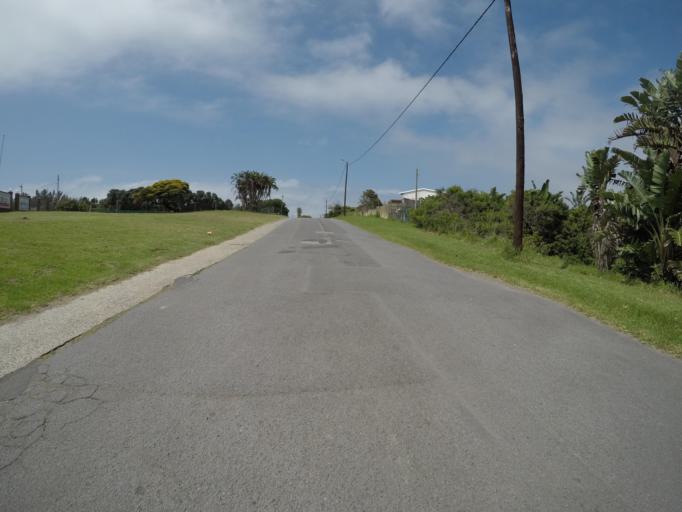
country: ZA
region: Eastern Cape
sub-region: Buffalo City Metropolitan Municipality
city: East London
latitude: -32.9378
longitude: 28.0232
